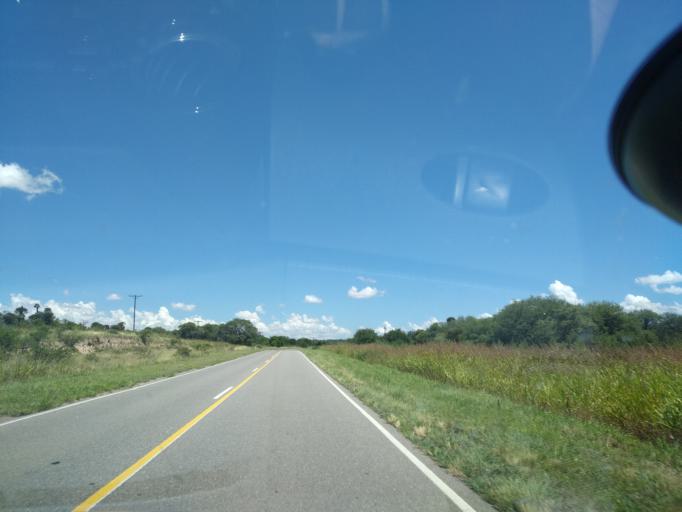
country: AR
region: Cordoba
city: Salsacate
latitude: -31.4168
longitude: -65.0950
